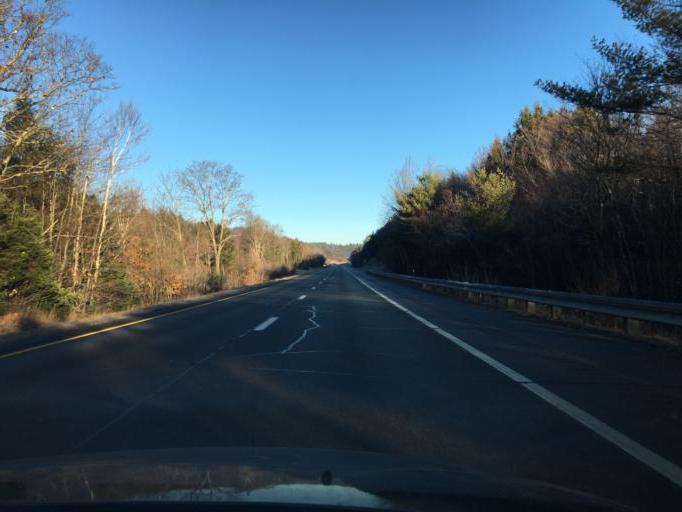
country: US
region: New Hampshire
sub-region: Belknap County
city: Sanbornton
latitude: 43.5663
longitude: -71.6196
